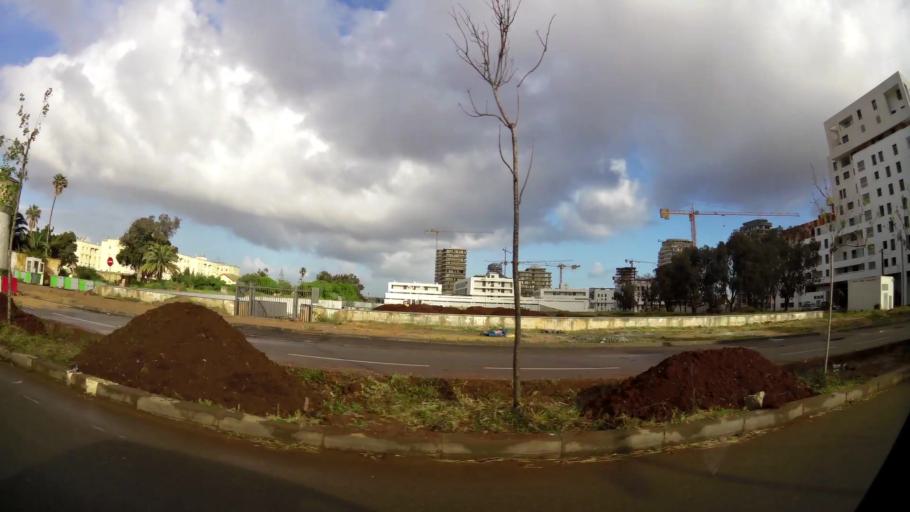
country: MA
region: Grand Casablanca
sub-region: Casablanca
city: Casablanca
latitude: 33.5573
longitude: -7.6526
